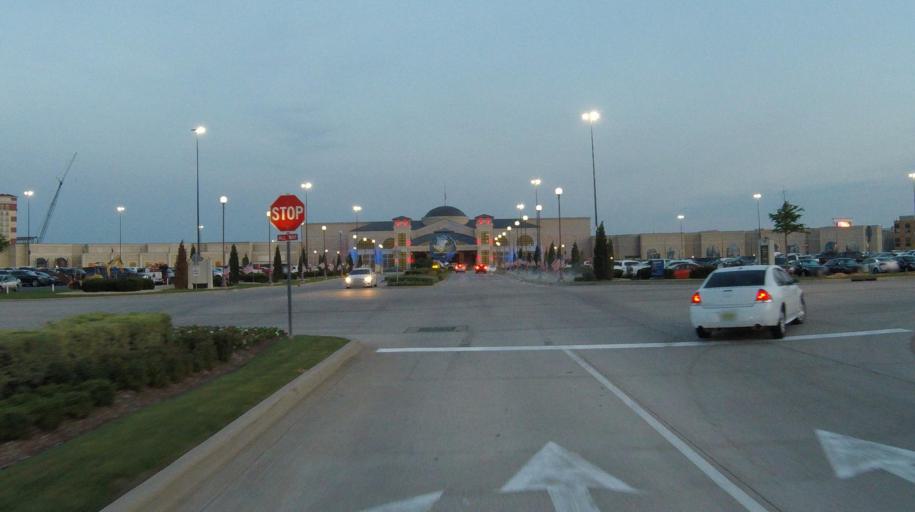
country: US
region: Texas
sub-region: Cooke County
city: Gainesville
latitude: 33.7623
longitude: -97.1304
